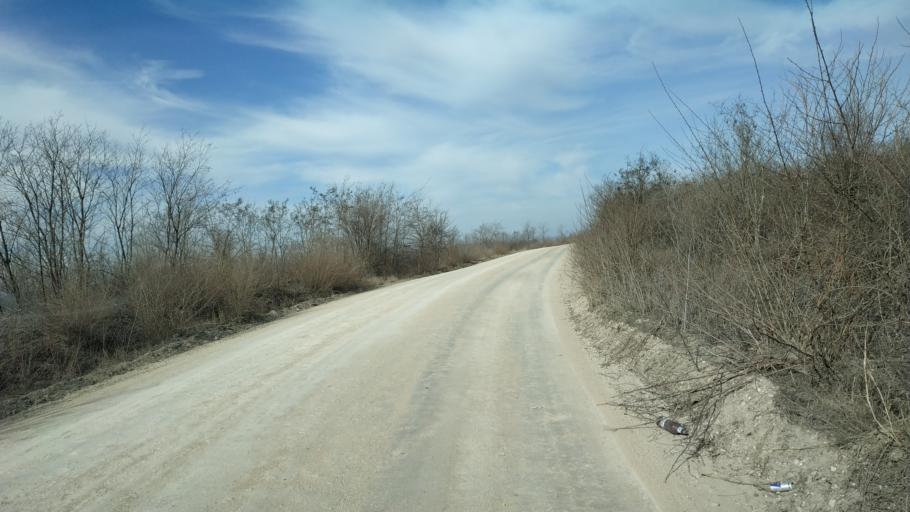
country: MD
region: Nisporeni
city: Nisporeni
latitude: 46.9664
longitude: 28.2008
